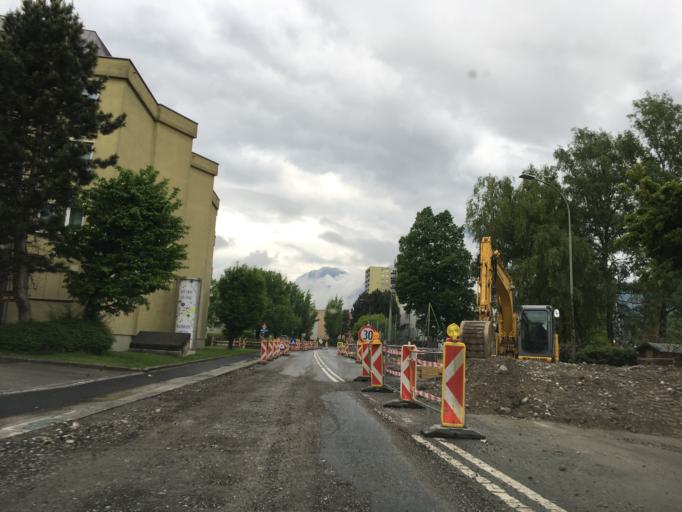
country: AT
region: Tyrol
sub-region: Politischer Bezirk Innsbruck Land
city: Ampass
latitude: 47.2743
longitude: 11.4367
